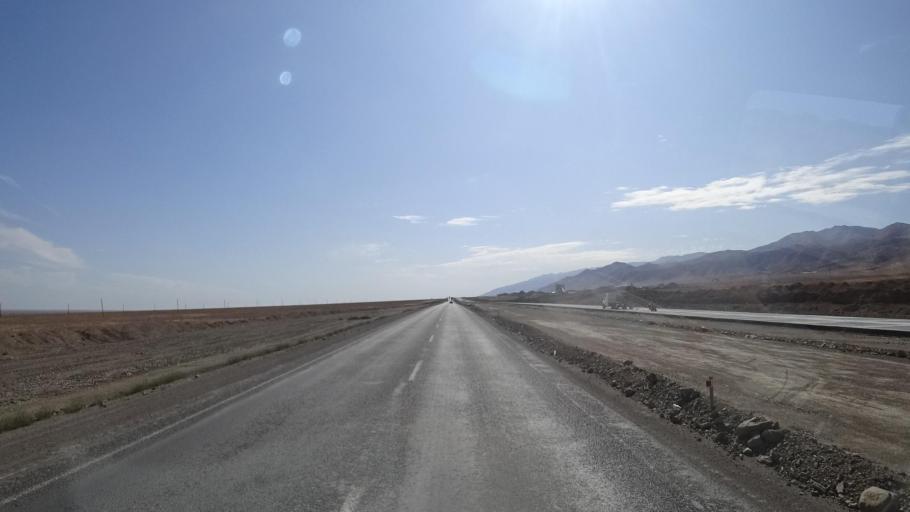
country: KG
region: Chuy
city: Ivanovka
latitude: 43.3946
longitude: 75.1300
